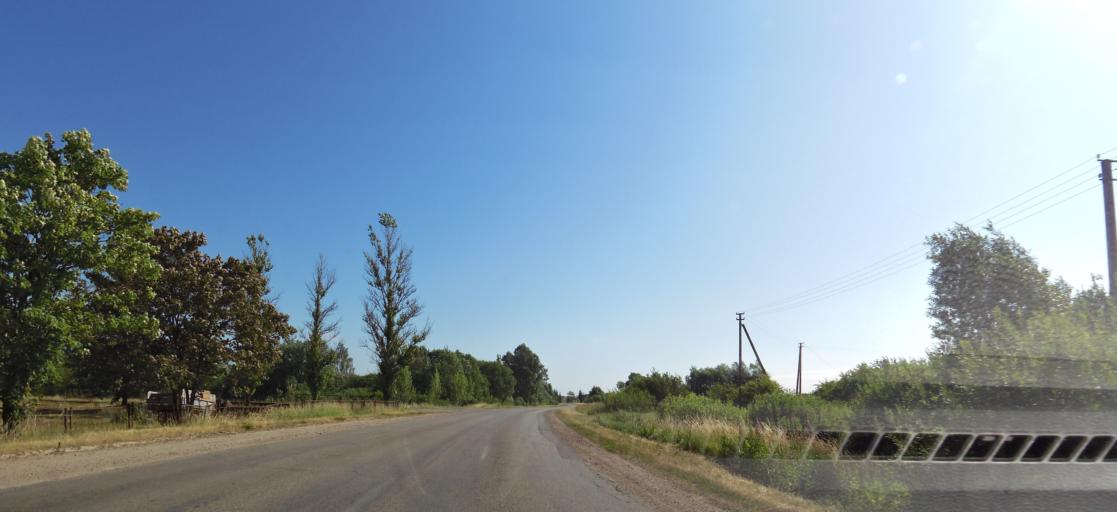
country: LT
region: Panevezys
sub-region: Birzai
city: Birzai
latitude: 56.2044
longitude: 24.7816
